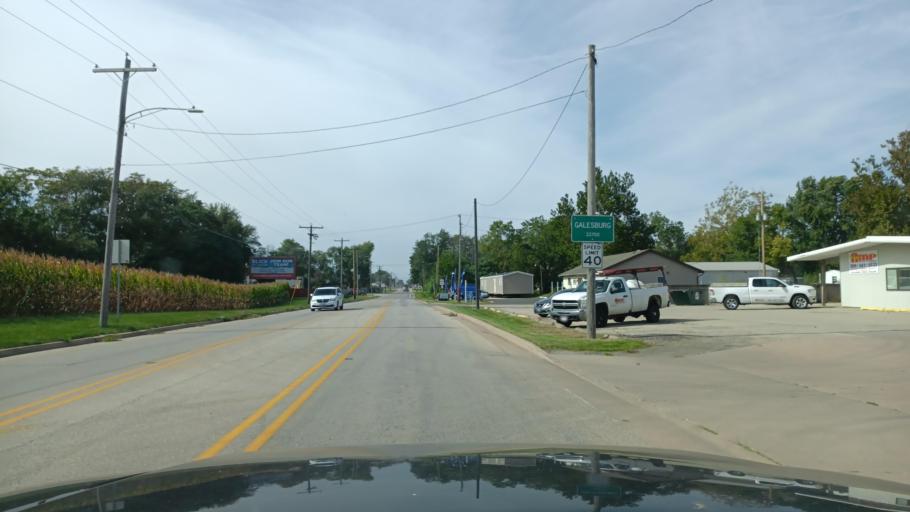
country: US
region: Illinois
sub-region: Knox County
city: Knoxville
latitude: 40.9287
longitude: -90.3271
